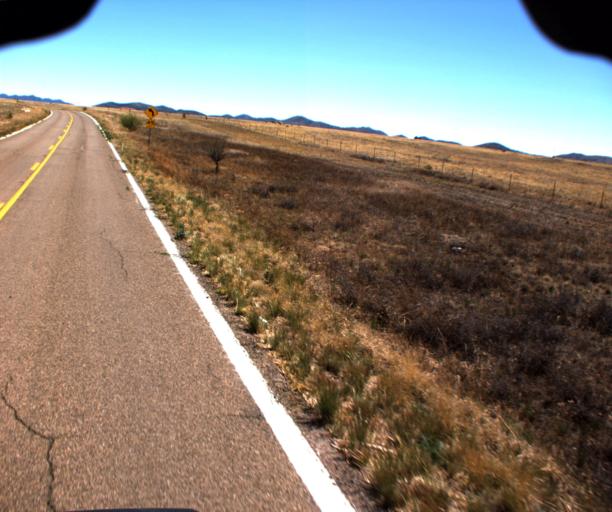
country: US
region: Arizona
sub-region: Cochise County
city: Huachuca City
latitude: 31.6243
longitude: -110.5920
